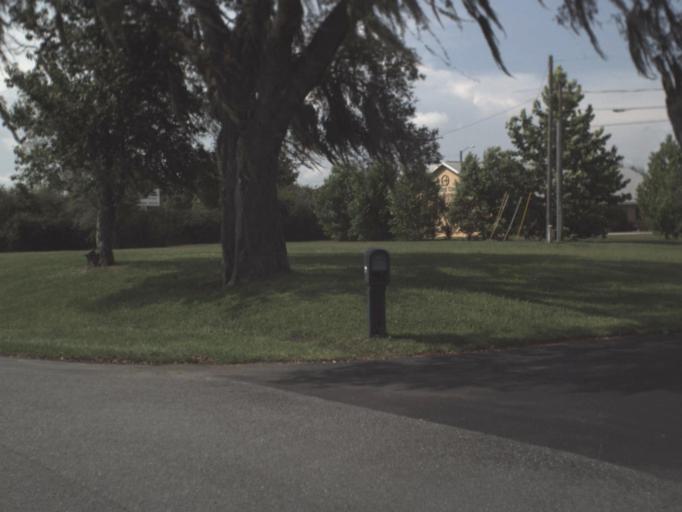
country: US
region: Florida
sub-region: Citrus County
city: Citrus Springs
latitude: 28.9745
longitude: -82.4245
